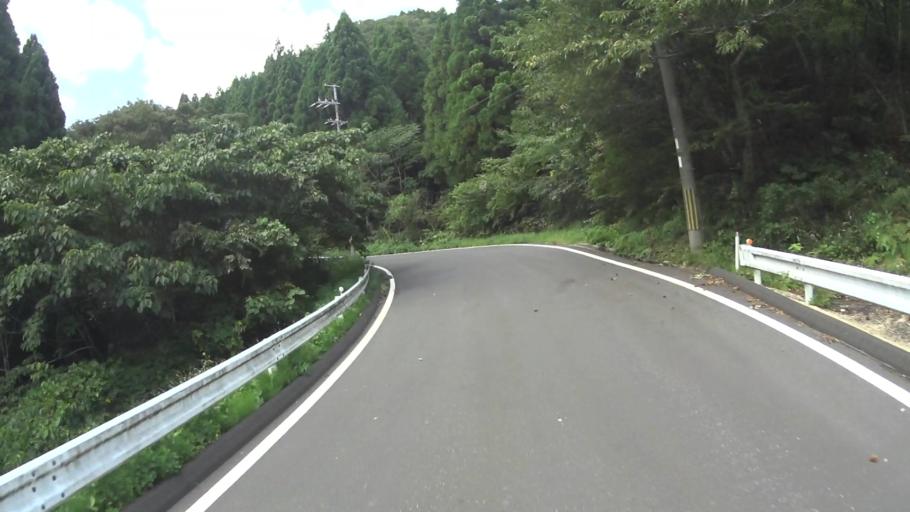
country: JP
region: Kyoto
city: Miyazu
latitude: 35.7288
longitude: 135.2047
